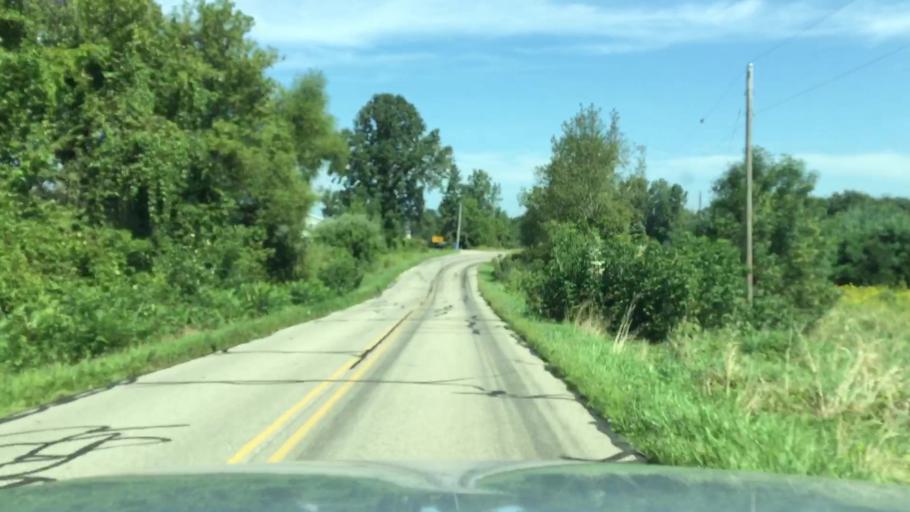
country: US
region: Michigan
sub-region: Lenawee County
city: Manitou Beach-Devils Lake
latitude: 41.9959
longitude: -84.3251
